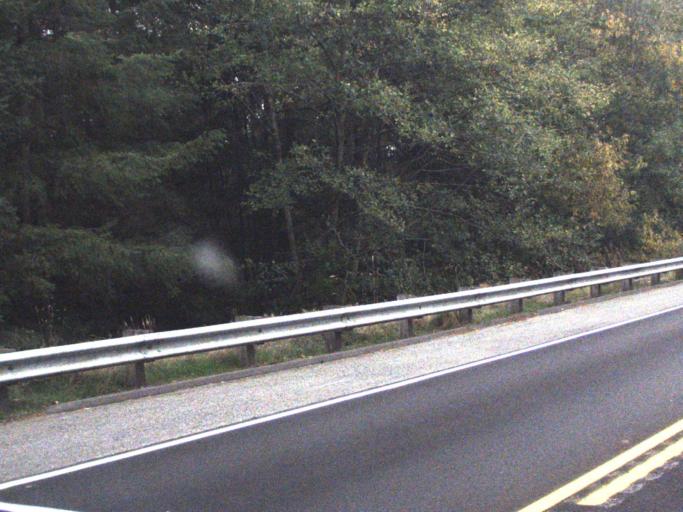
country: US
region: Washington
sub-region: Island County
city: Freeland
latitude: 48.0509
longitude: -122.5669
